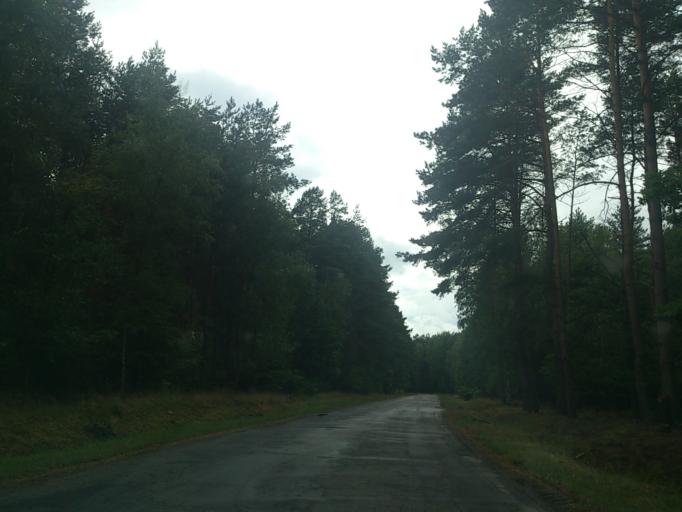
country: PL
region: Greater Poland Voivodeship
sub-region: Powiat gnieznienski
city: Kiszkowo
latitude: 52.5204
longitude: 17.1707
